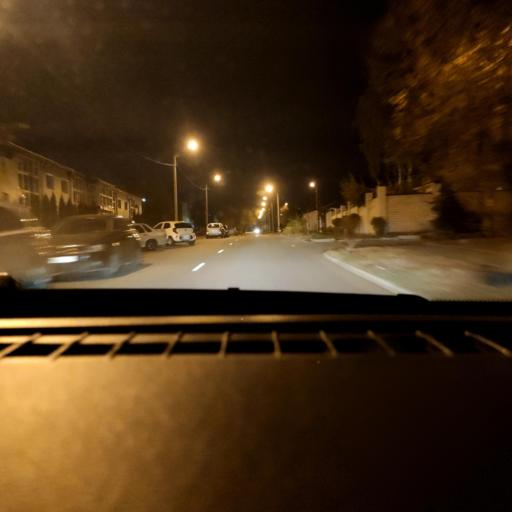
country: RU
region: Voronezj
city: Pridonskoy
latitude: 51.6627
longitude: 39.1232
